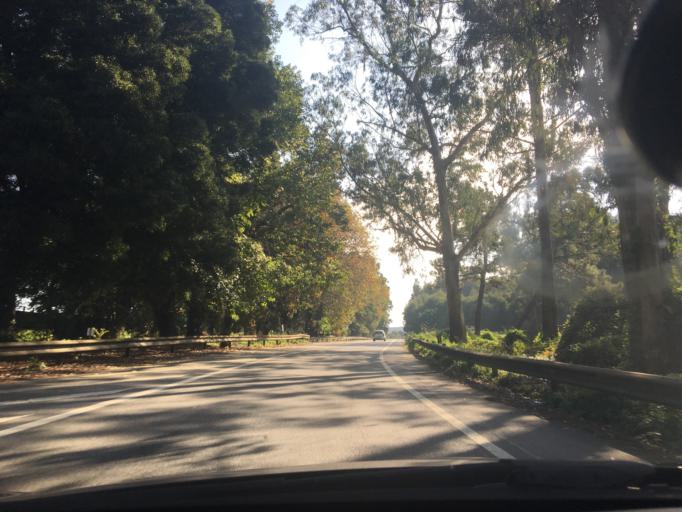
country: PT
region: Porto
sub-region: Maia
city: Maia
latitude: 41.2236
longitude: -8.6276
